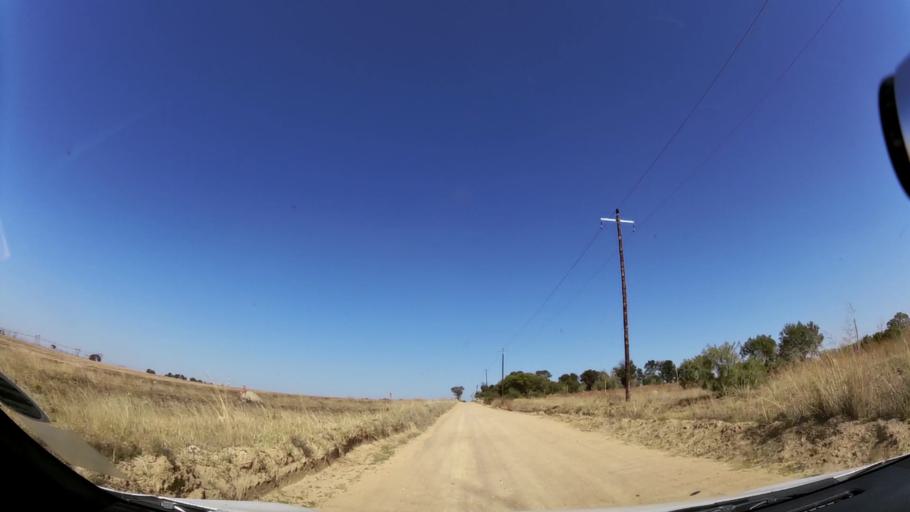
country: ZA
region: Gauteng
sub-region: City of Johannesburg Metropolitan Municipality
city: Diepsloot
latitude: -25.9134
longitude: 28.0705
